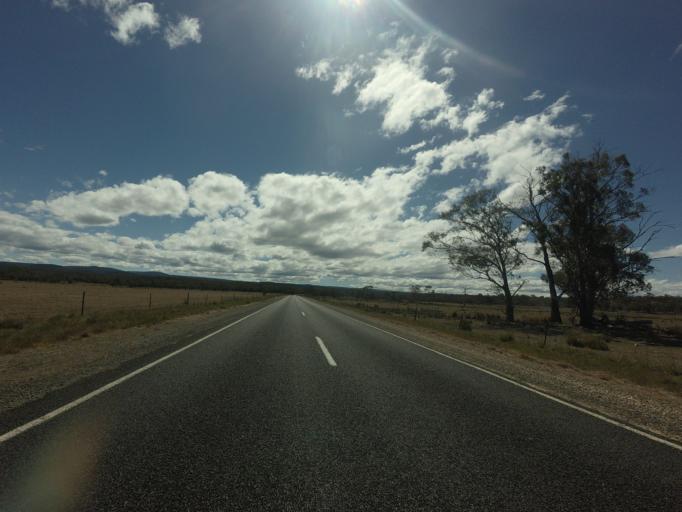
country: AU
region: Tasmania
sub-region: Break O'Day
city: St Helens
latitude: -42.0433
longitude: 148.0356
